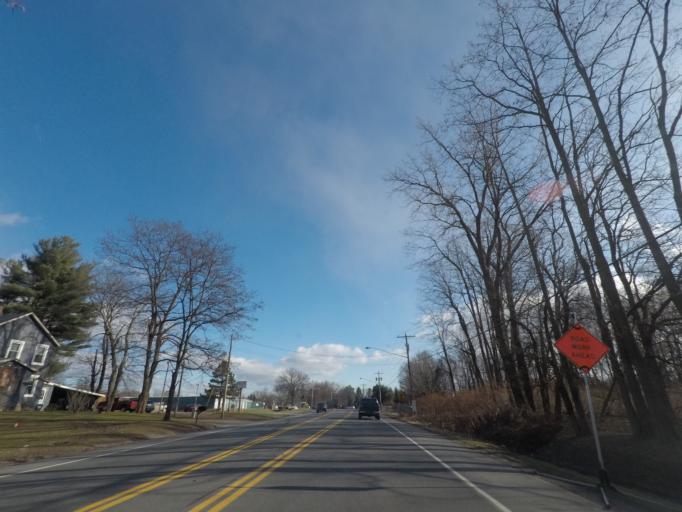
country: US
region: New York
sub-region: Albany County
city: Colonie
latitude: 42.7290
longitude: -73.8586
